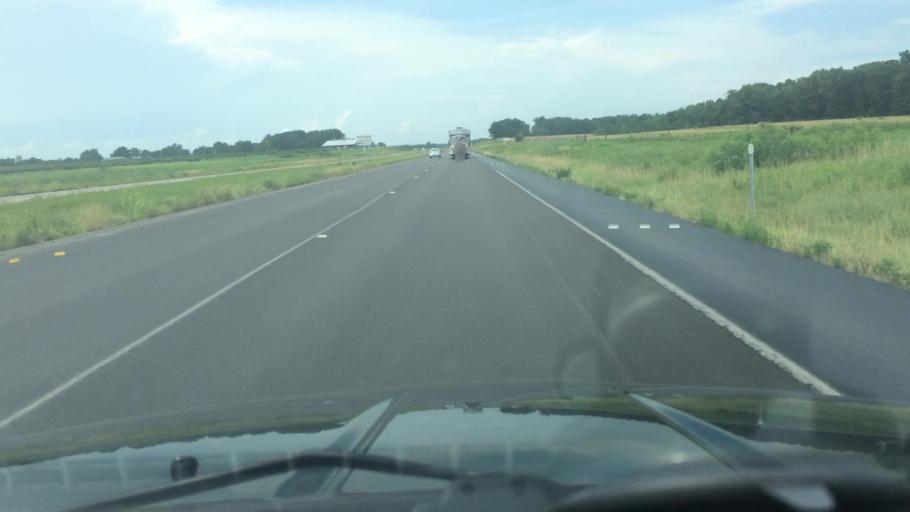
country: US
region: Missouri
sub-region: Saint Clair County
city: Osceola
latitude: 37.9744
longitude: -93.6474
